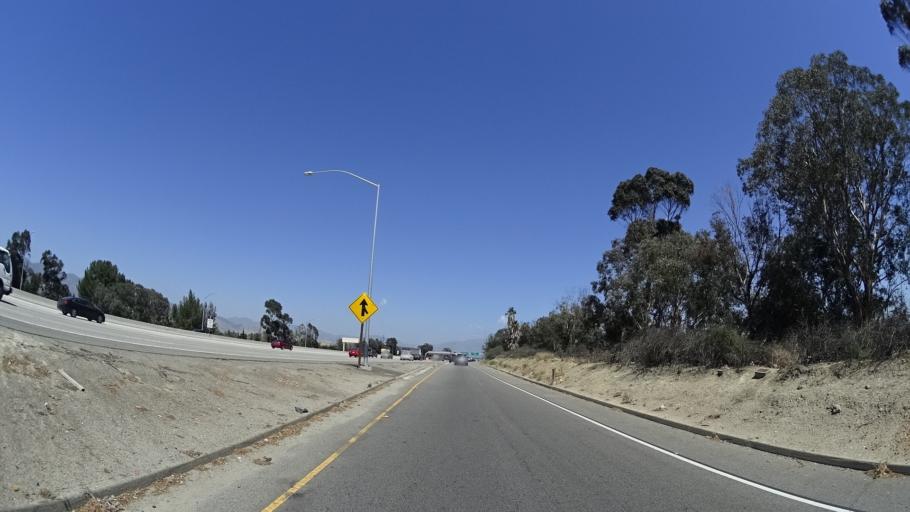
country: US
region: California
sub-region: Los Angeles County
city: San Fernando
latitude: 34.2656
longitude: -118.4655
